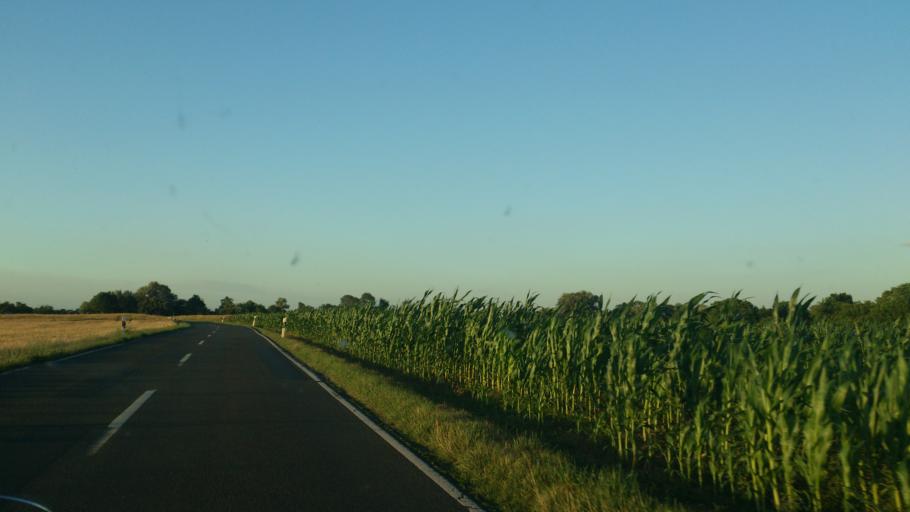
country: DE
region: Hesse
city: Raunheim
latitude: 50.0199
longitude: 8.4438
